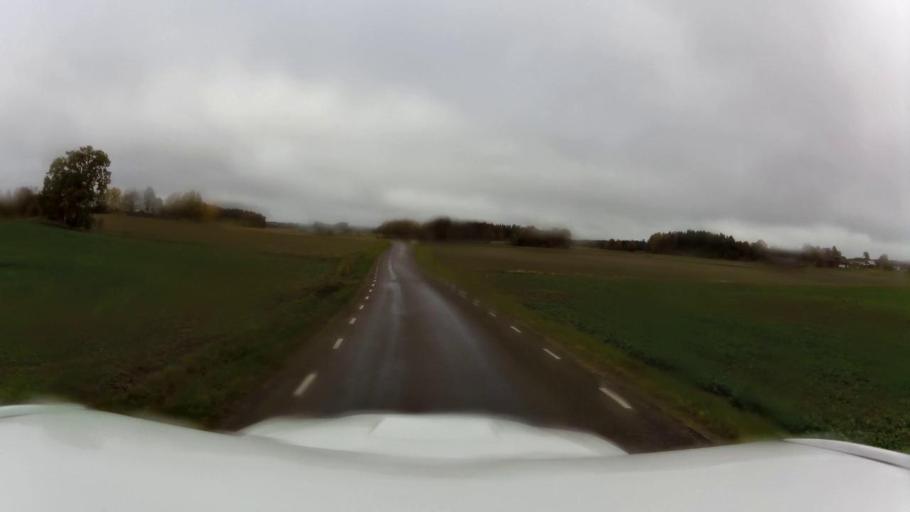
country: SE
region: OEstergoetland
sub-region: Linkopings Kommun
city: Linghem
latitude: 58.4572
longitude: 15.8301
